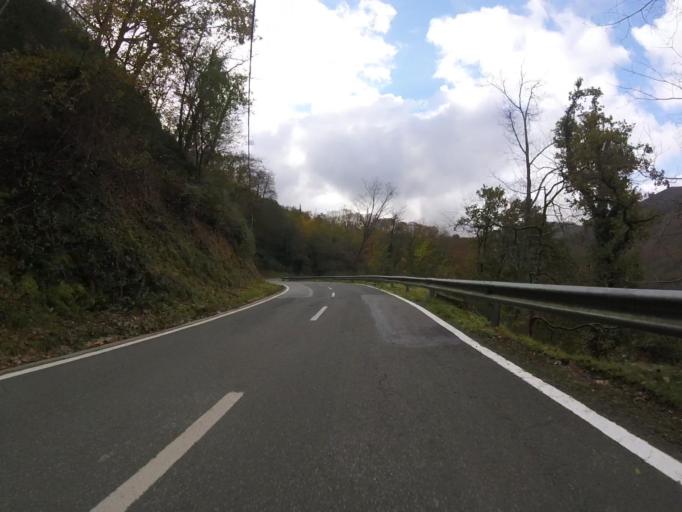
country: ES
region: Navarre
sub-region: Provincia de Navarra
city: Goizueta
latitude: 43.2056
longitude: -1.8562
